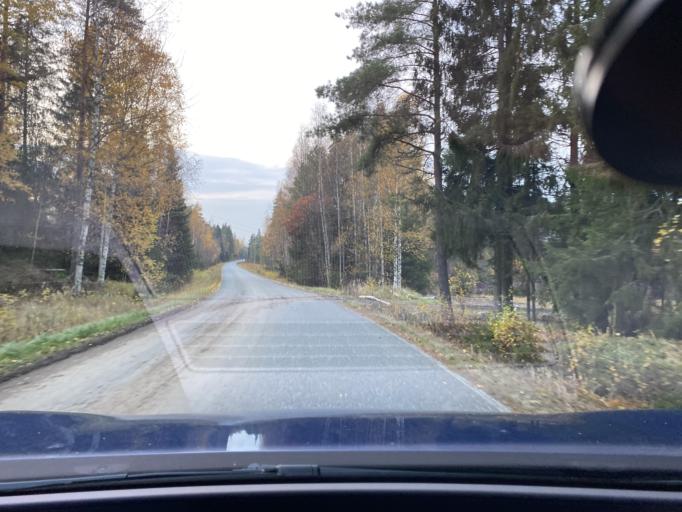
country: FI
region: Varsinais-Suomi
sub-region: Loimaa
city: Alastaro
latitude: 61.0839
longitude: 22.9304
